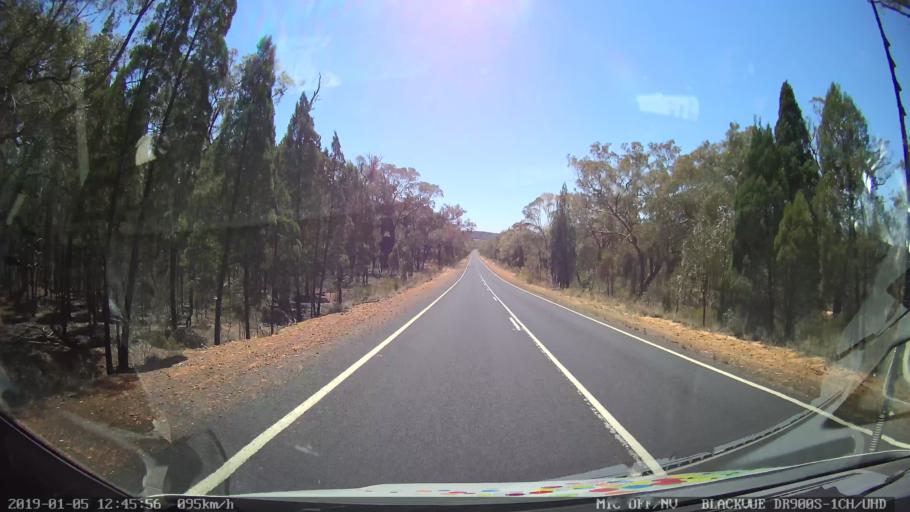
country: AU
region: New South Wales
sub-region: Warrumbungle Shire
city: Coonabarabran
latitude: -31.1230
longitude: 149.5561
